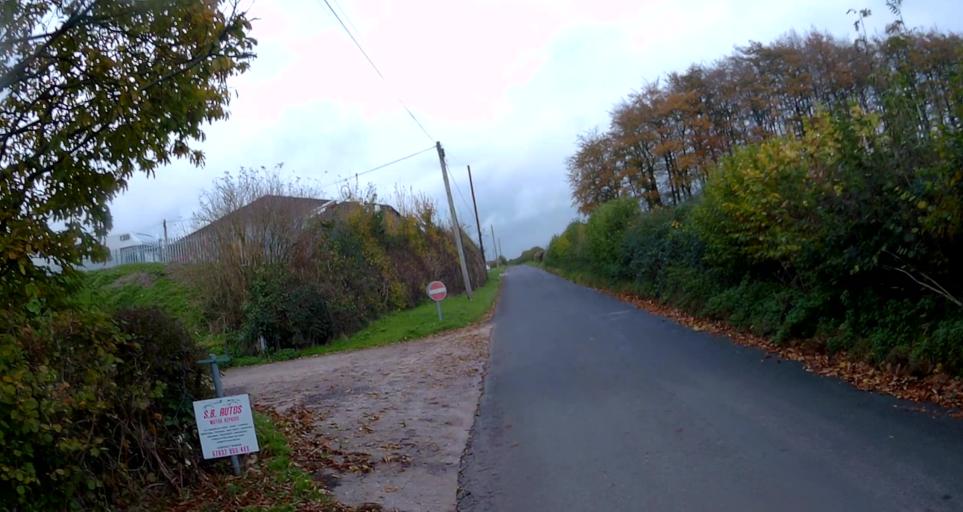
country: GB
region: England
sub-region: Hampshire
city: Four Marks
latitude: 51.1720
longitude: -1.0426
